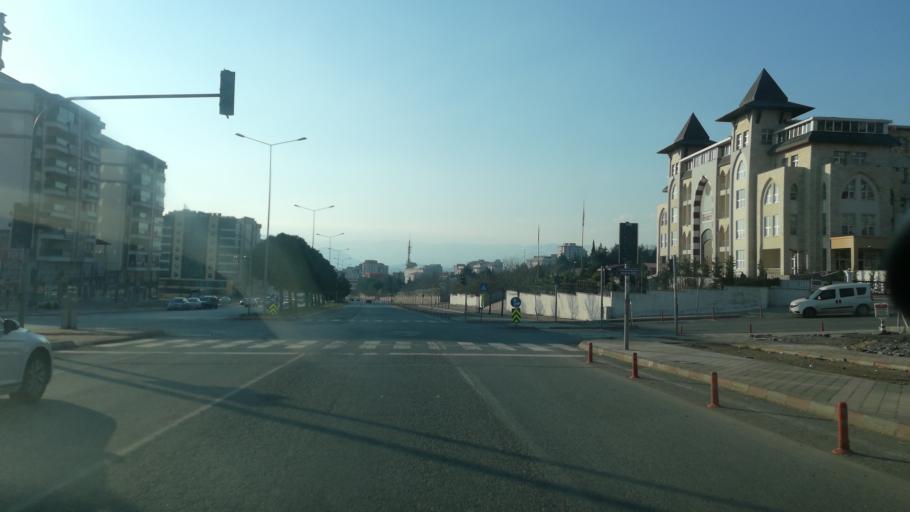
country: TR
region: Kahramanmaras
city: Kahramanmaras
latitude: 37.5995
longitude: 36.8380
